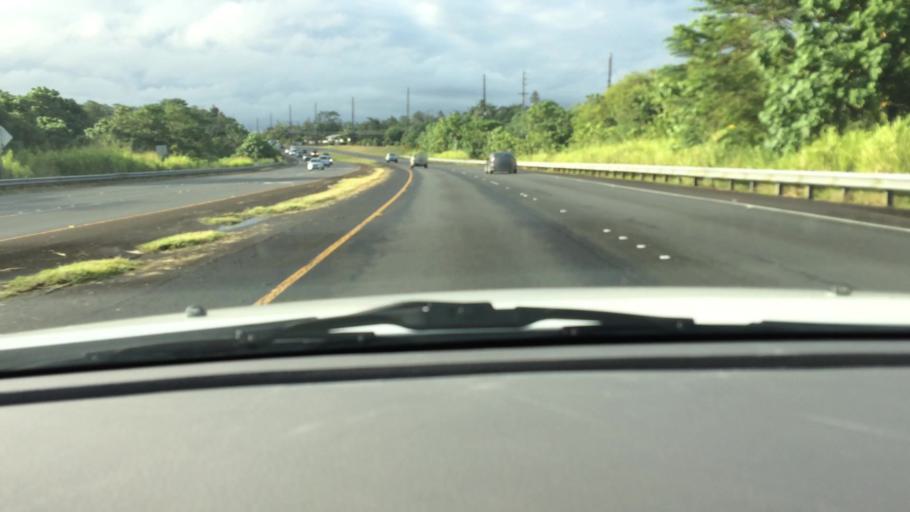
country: US
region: Hawaii
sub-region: Hawaii County
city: Kea'au
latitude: 19.6092
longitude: -155.0295
